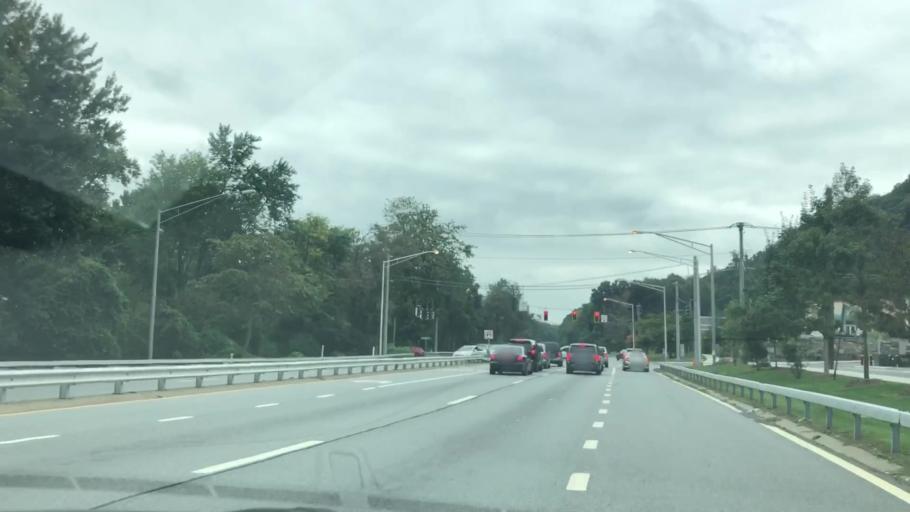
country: US
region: New York
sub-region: Westchester County
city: Ardsley
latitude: 41.0033
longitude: -73.8562
